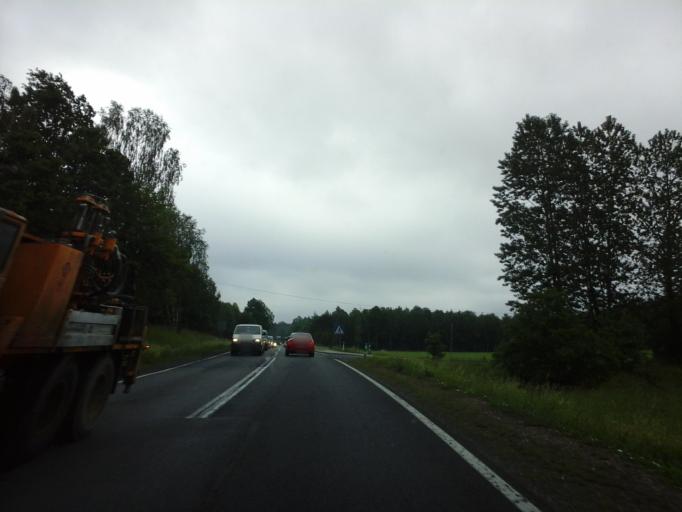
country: PL
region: West Pomeranian Voivodeship
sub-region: Powiat walecki
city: Miroslawiec
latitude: 53.3318
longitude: 16.0554
